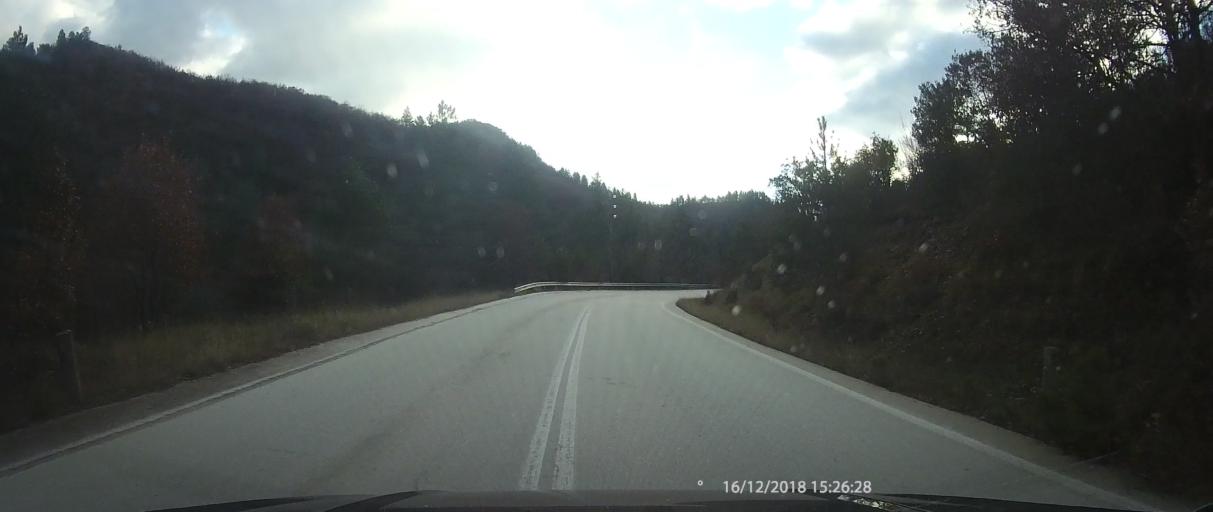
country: GR
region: Epirus
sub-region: Nomos Ioanninon
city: Konitsa
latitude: 40.1169
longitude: 20.7795
